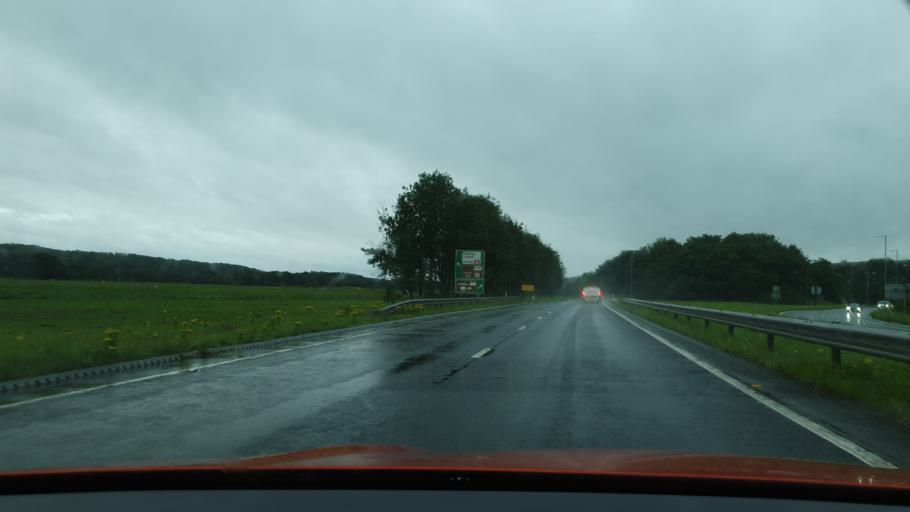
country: GB
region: England
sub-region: Cumbria
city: Arnside
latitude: 54.2275
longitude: -2.8681
